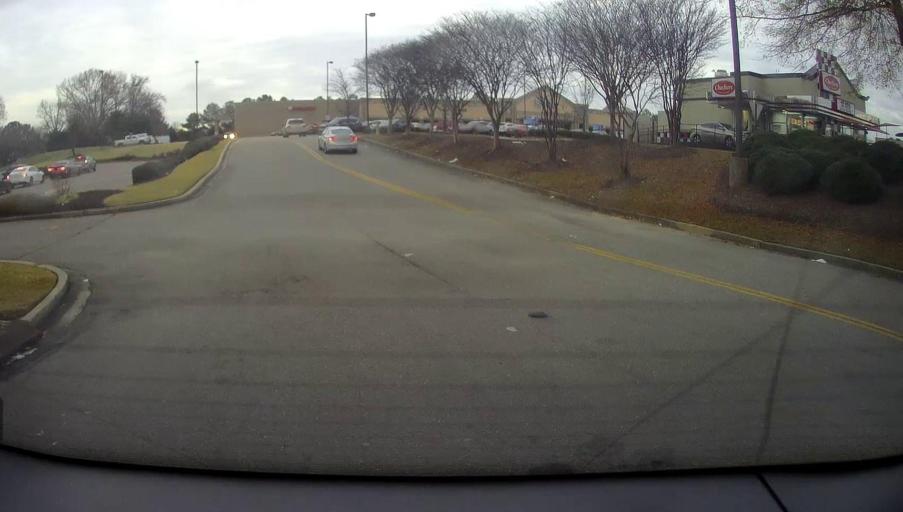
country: US
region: Tennessee
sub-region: Shelby County
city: Germantown
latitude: 35.0489
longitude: -89.7986
